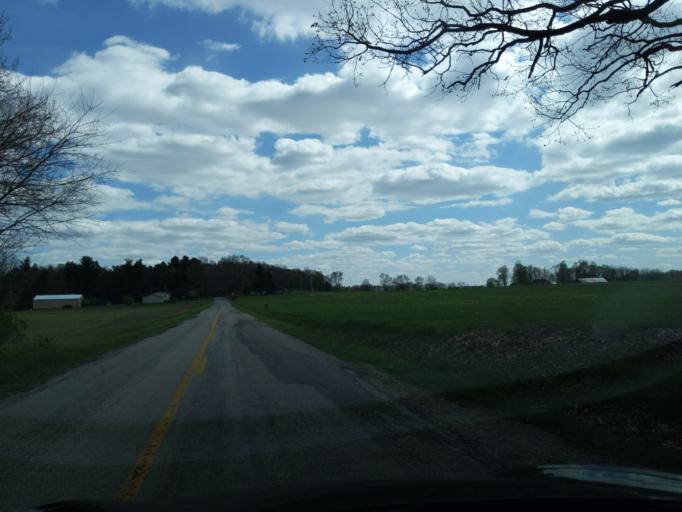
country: US
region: Michigan
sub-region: Ingham County
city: Leslie
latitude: 42.4546
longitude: -84.5460
